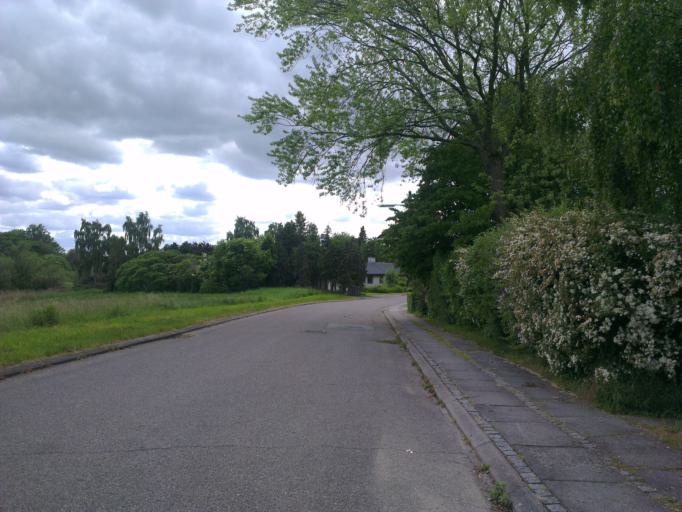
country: DK
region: Capital Region
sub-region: Frederikssund Kommune
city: Slangerup
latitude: 55.8496
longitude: 12.1789
